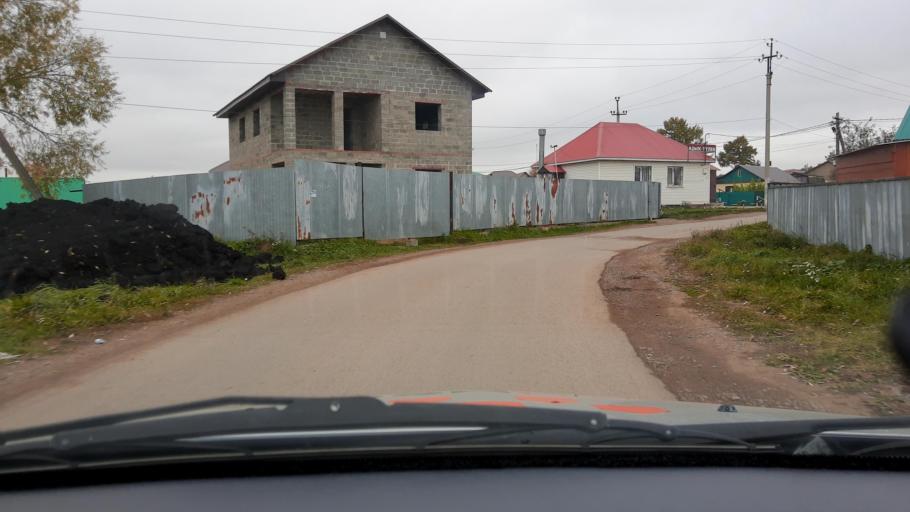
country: RU
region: Bashkortostan
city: Mikhaylovka
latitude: 54.8022
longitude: 55.8842
